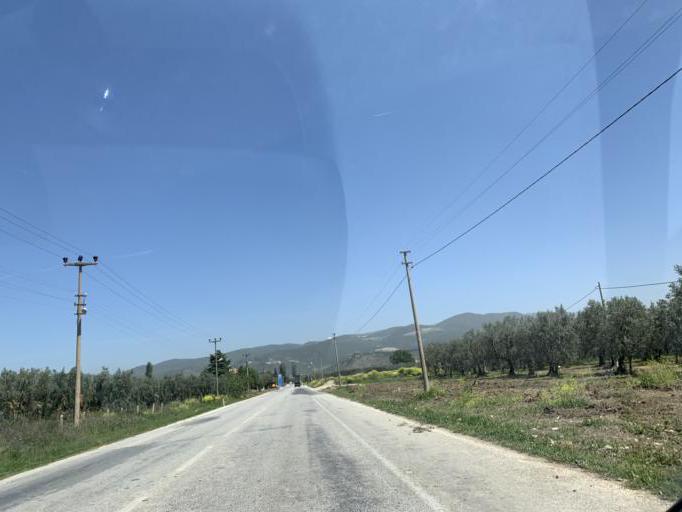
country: TR
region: Bursa
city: Iznik
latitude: 40.4170
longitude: 29.7146
